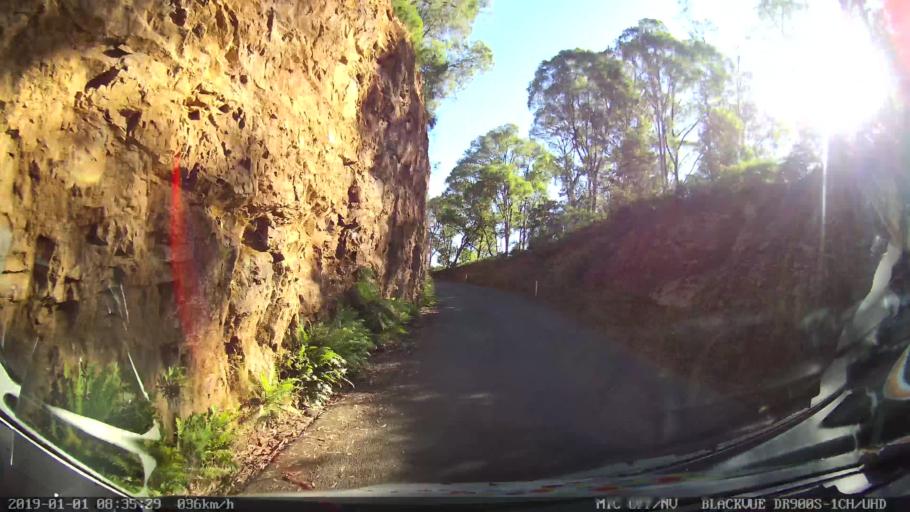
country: AU
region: New South Wales
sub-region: Snowy River
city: Jindabyne
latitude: -36.3488
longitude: 148.1937
